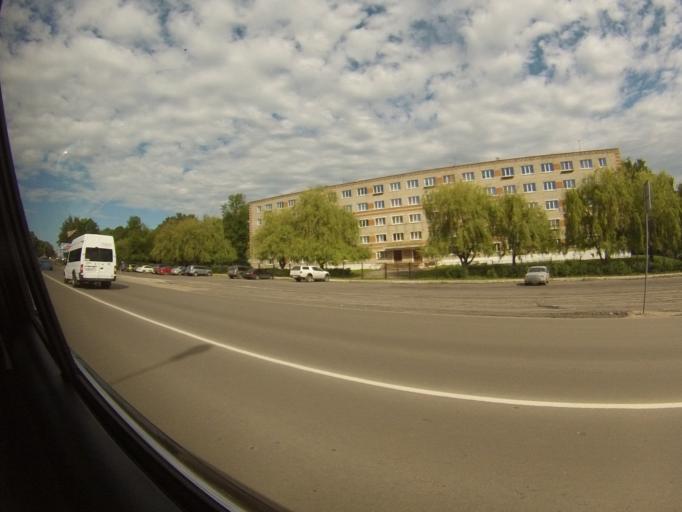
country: RU
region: Orjol
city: Mtsensk
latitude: 53.2877
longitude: 36.5915
